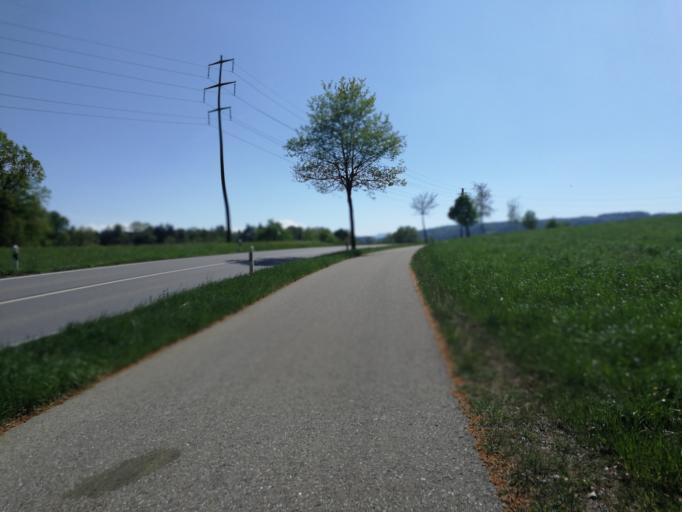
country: CH
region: Zurich
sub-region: Bezirk Uster
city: Moenchaltorf / Dorf
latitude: 47.2994
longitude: 8.7207
